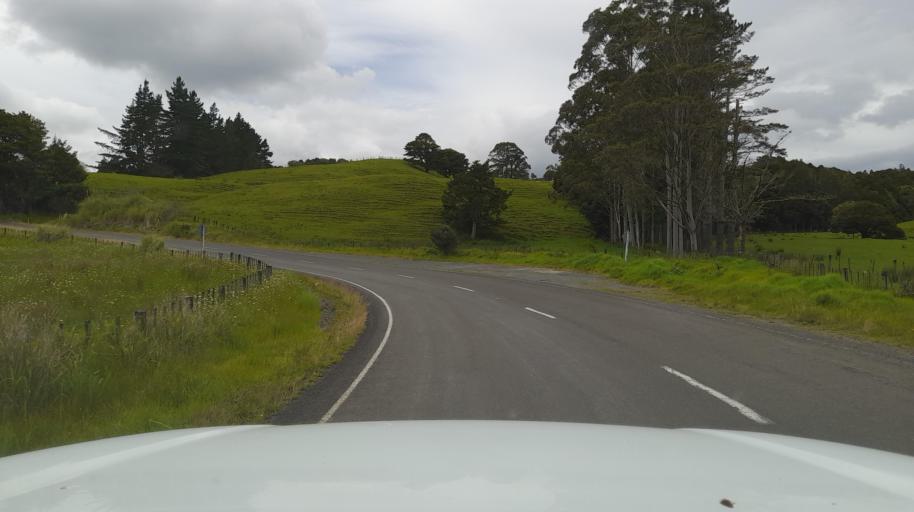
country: NZ
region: Northland
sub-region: Far North District
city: Kaitaia
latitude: -35.3596
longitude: 173.4831
